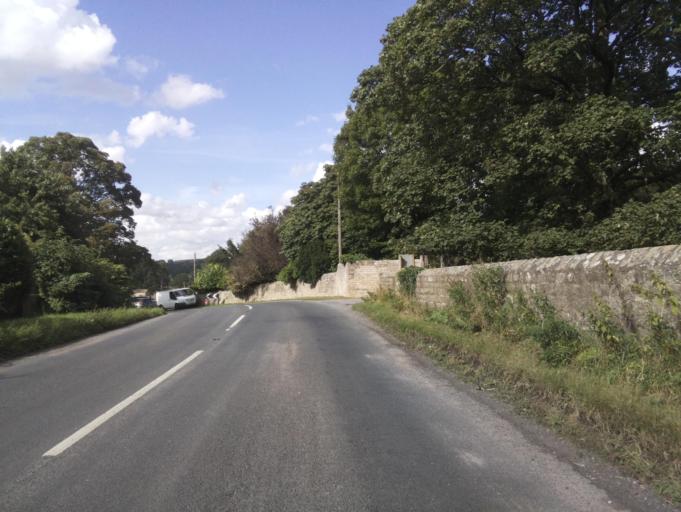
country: GB
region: England
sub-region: North Yorkshire
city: Leyburn
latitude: 54.2669
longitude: -1.7417
